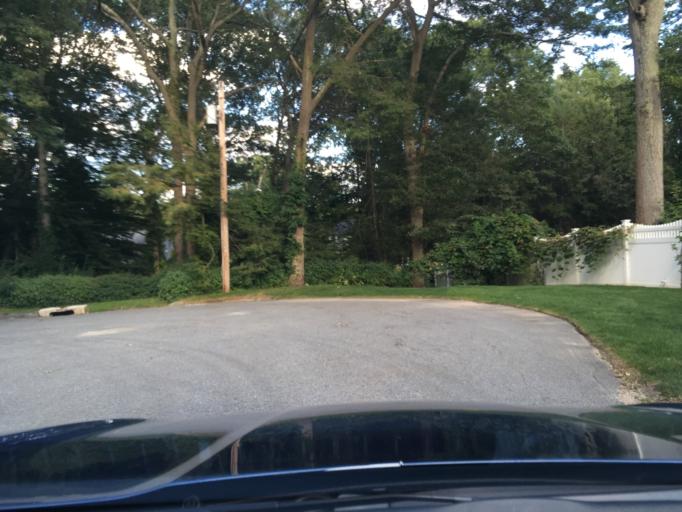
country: US
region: Rhode Island
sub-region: Kent County
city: East Greenwich
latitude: 41.6413
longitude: -71.4780
